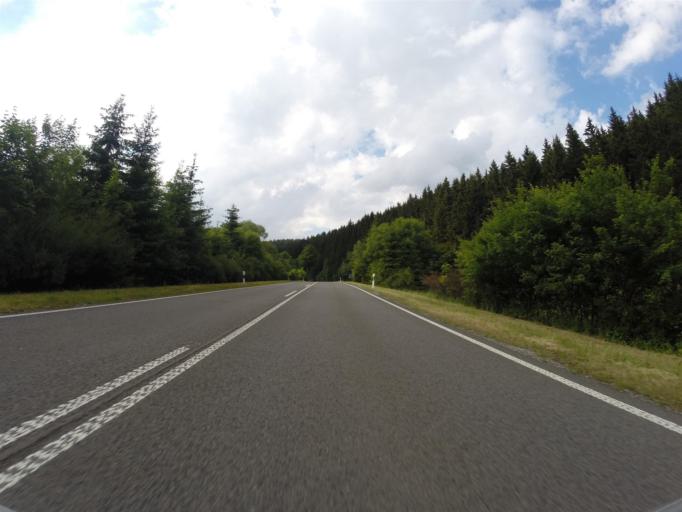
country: DE
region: Thuringia
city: Stutzerbach
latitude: 50.6439
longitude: 10.8554
